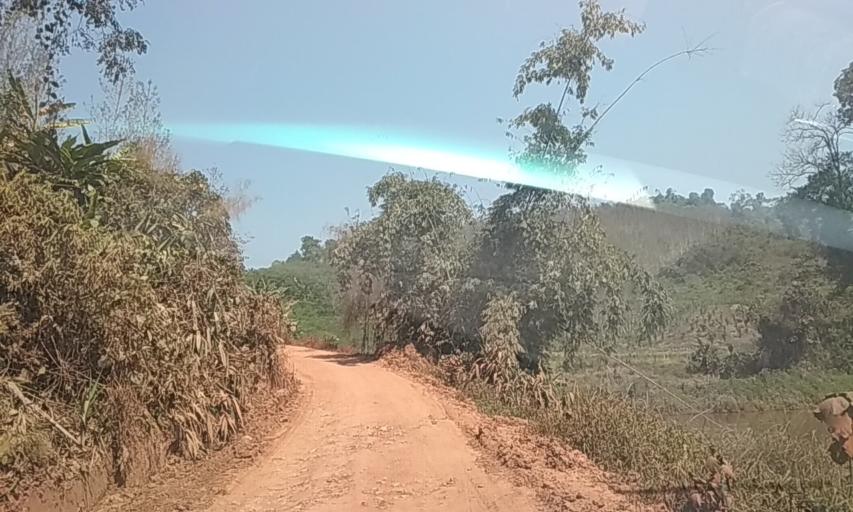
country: CN
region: Yunnan
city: Mengla
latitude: 21.5222
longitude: 101.8440
